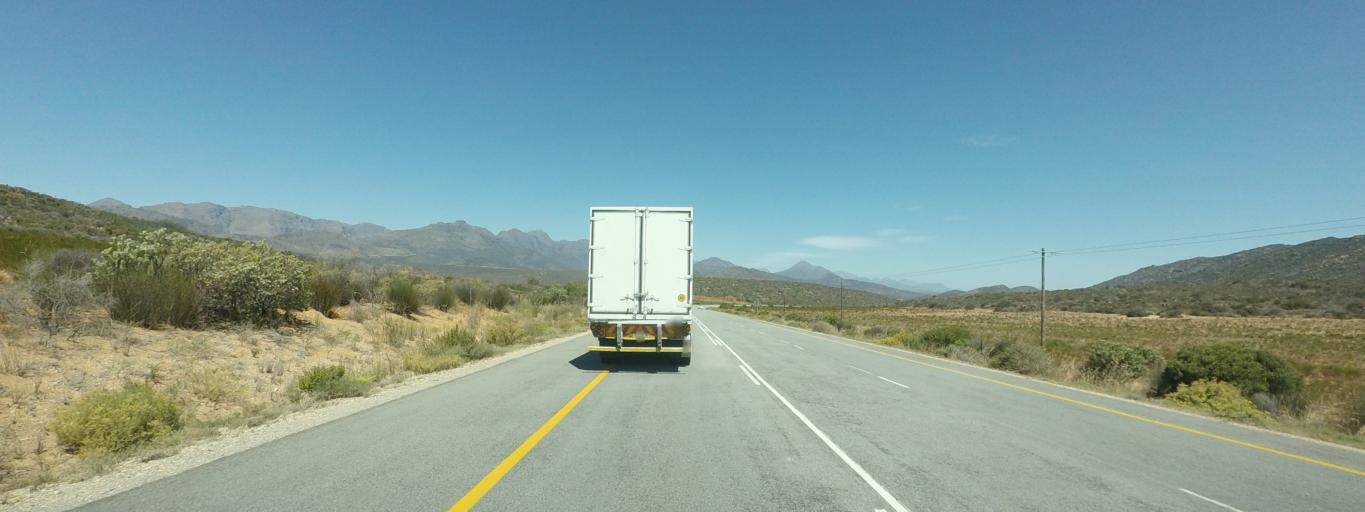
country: ZA
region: Western Cape
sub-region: West Coast District Municipality
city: Clanwilliam
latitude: -32.3247
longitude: 18.9194
